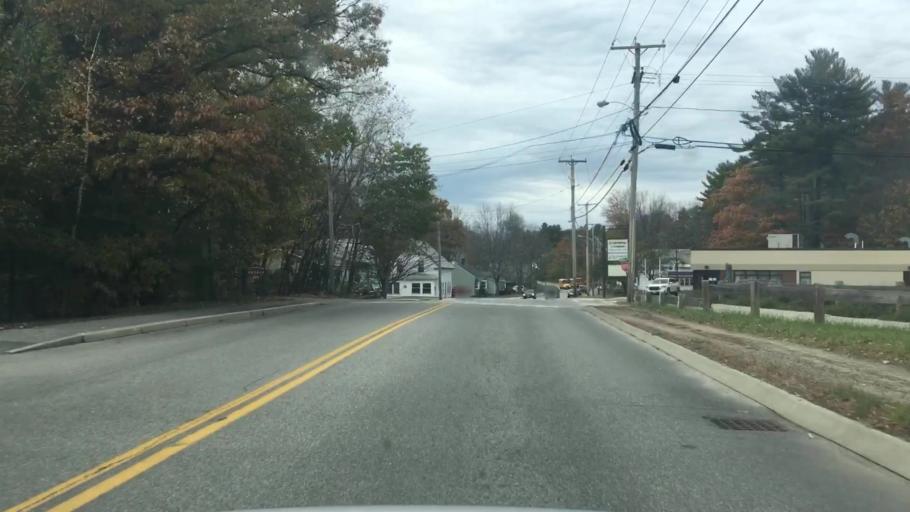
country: US
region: Maine
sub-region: York County
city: Springvale
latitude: 43.4625
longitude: -70.7856
